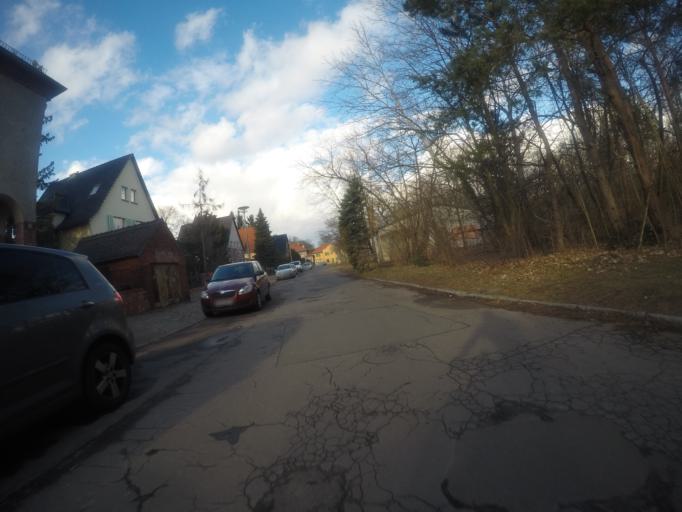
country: DE
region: Berlin
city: Oberschoneweide
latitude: 52.4759
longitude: 13.5112
